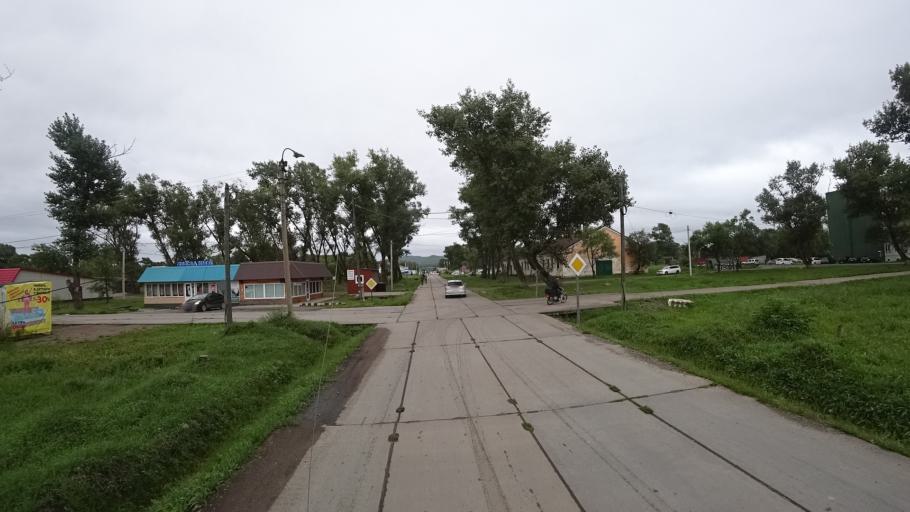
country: RU
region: Primorskiy
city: Chernigovka
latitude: 44.3317
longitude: 132.5335
